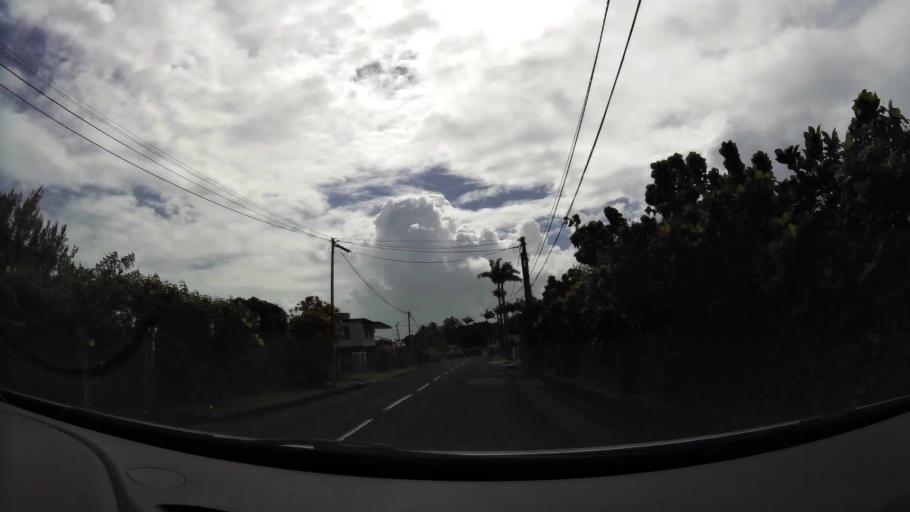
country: MQ
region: Martinique
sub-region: Martinique
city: Saint-Joseph
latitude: 14.6412
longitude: -61.0424
